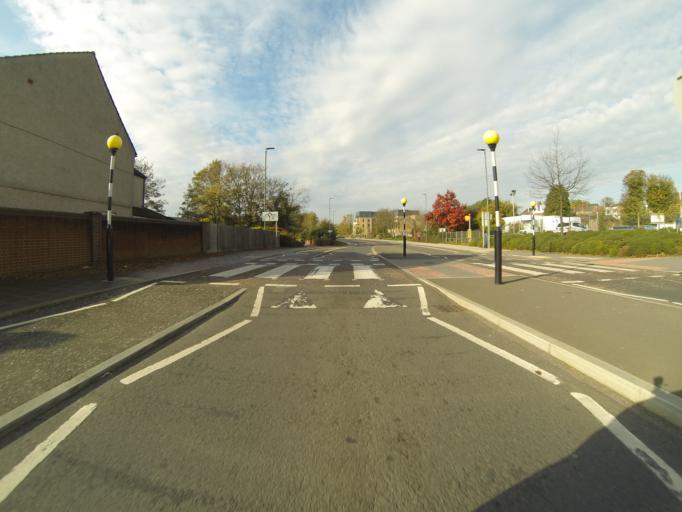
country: GB
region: England
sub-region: Greater London
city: Bexleyheath
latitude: 51.4557
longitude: 0.1427
